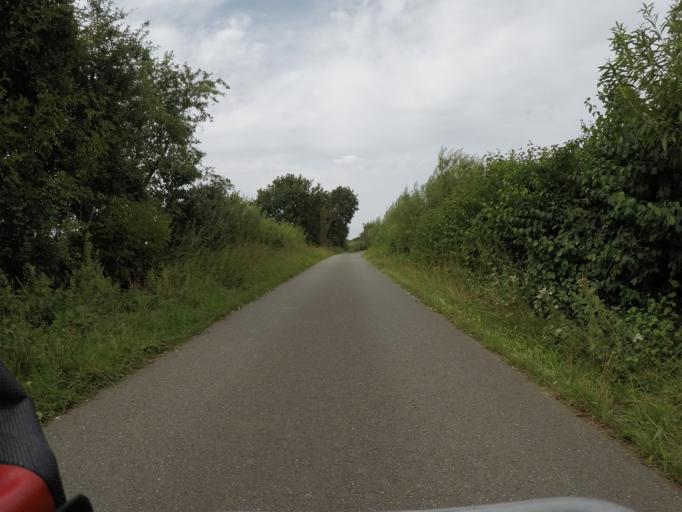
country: DE
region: Lower Saxony
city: Winsen
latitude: 53.3833
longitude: 10.2234
